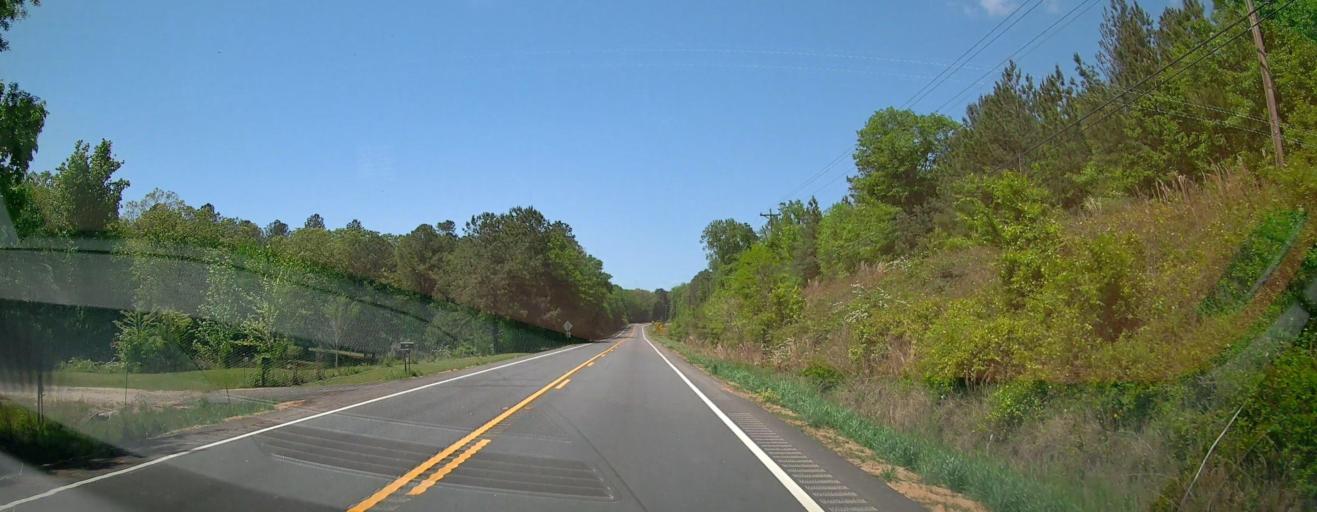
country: US
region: Georgia
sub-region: Putnam County
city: Eatonton
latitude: 33.2300
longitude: -83.4329
